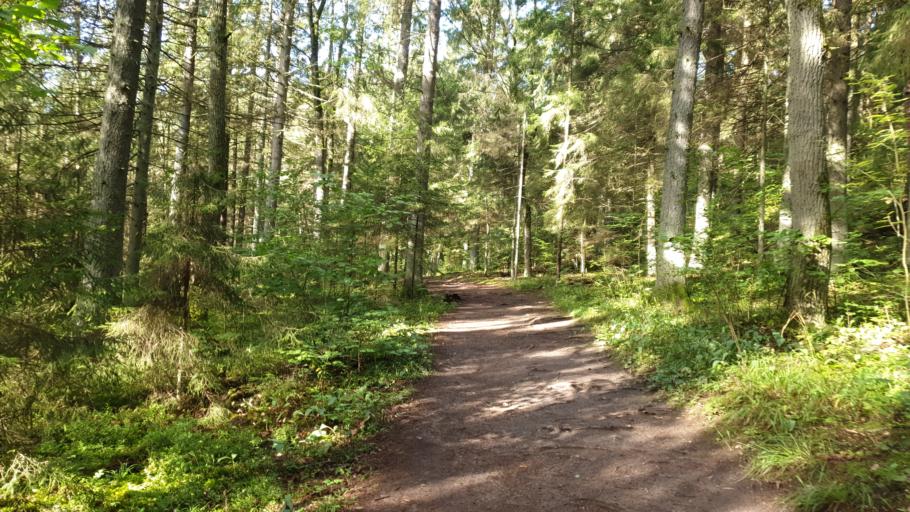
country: LT
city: Trakai
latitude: 54.6437
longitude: 24.9747
